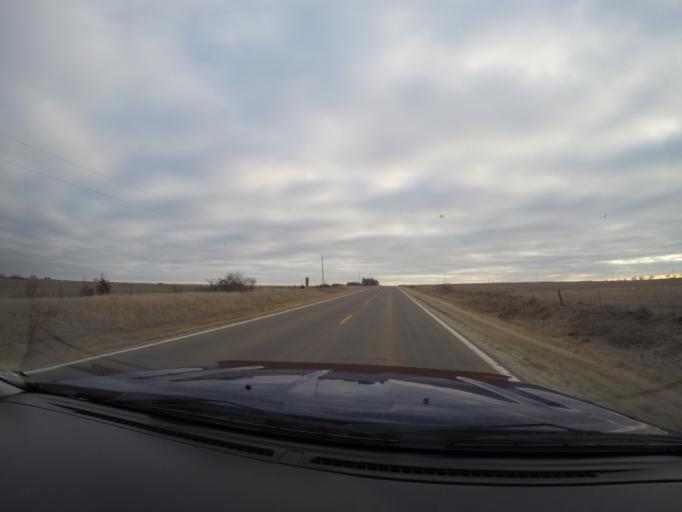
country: US
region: Kansas
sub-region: Morris County
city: Council Grove
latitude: 38.7992
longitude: -96.5013
